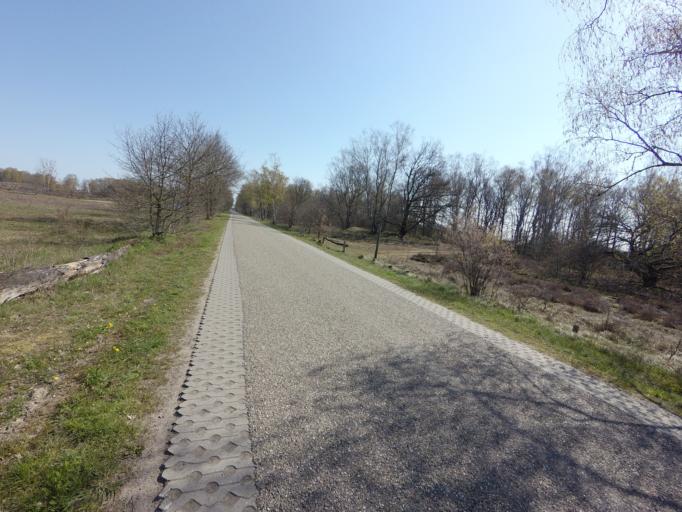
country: NL
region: Limburg
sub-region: Gemeente Bergen
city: Wellerlooi
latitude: 51.6040
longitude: 6.0696
